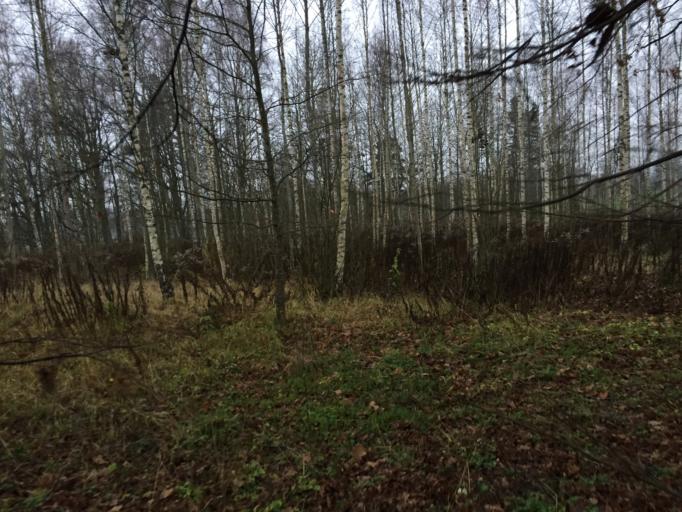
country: LV
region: Koceni
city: Koceni
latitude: 57.5517
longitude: 25.3585
